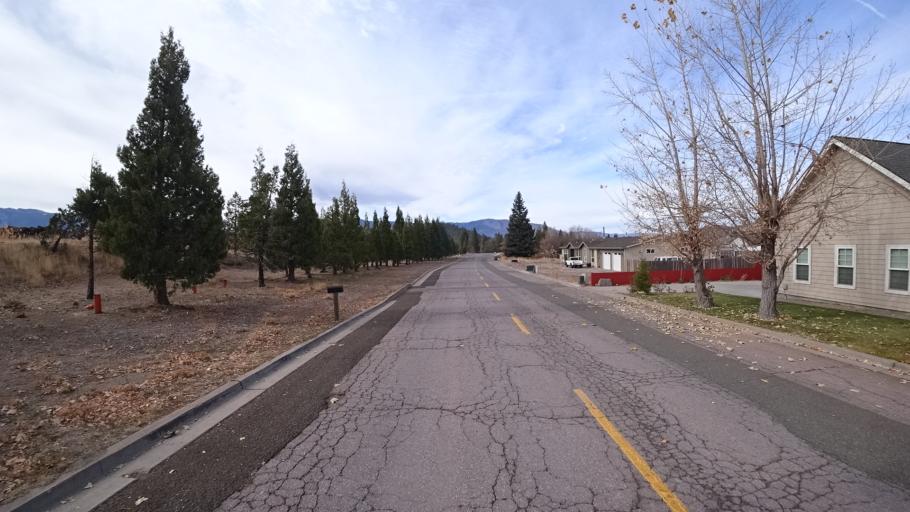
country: US
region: California
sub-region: Siskiyou County
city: Weed
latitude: 41.4360
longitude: -122.3798
